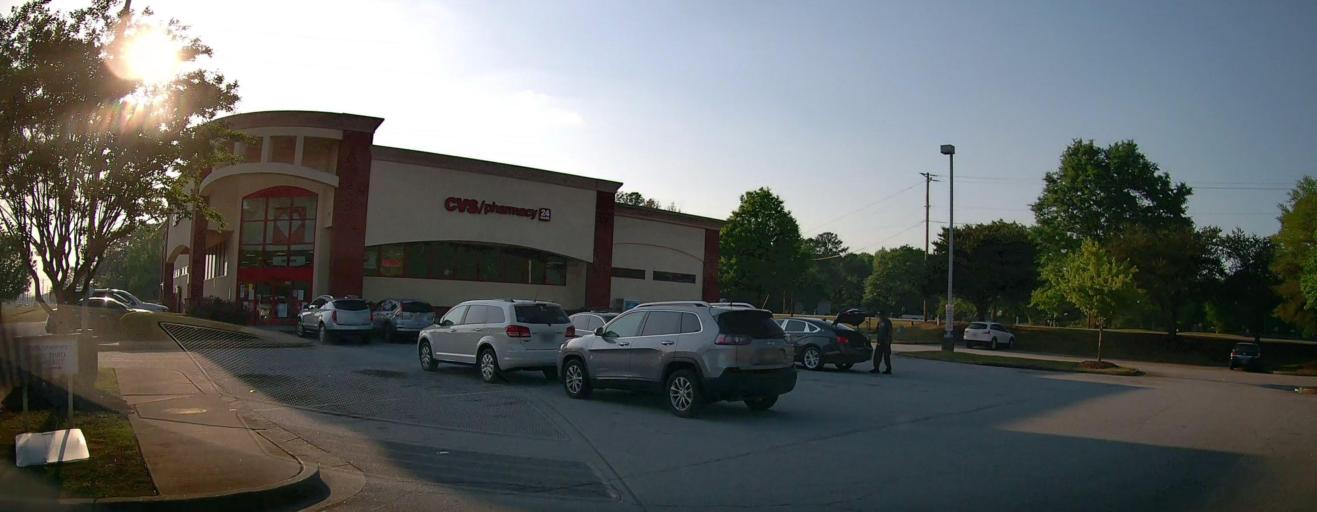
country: US
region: Georgia
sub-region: Newton County
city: Covington
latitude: 33.6034
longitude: -83.8503
